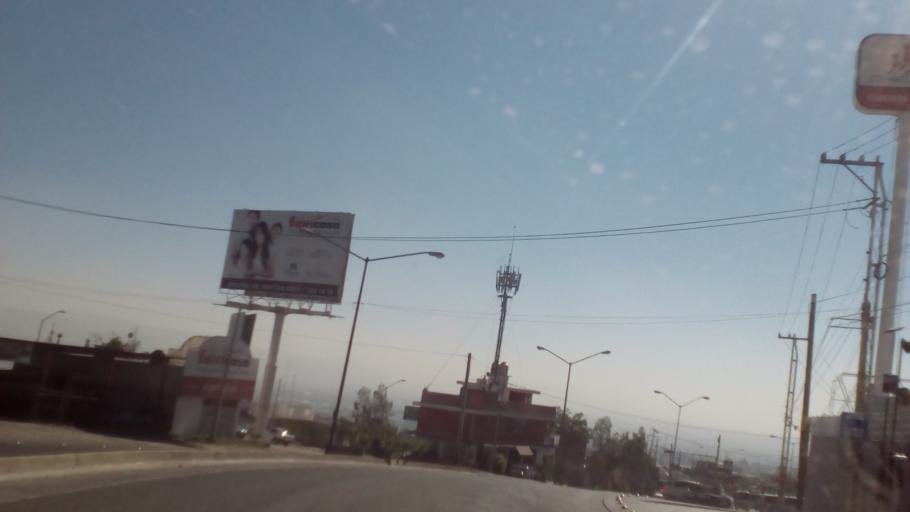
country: MX
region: Guanajuato
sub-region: Leon
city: La Ermita
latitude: 21.1352
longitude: -101.7180
